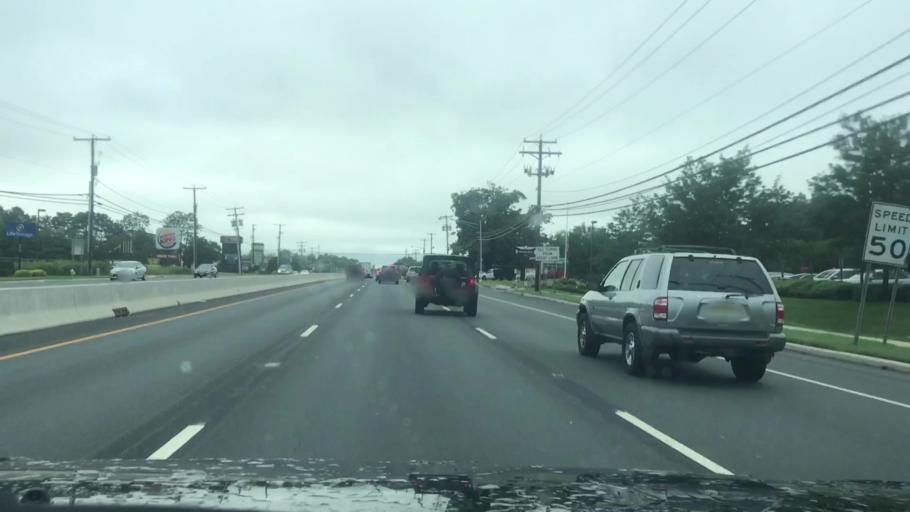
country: US
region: New Jersey
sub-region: Ocean County
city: Holiday City South
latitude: 39.9706
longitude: -74.2345
